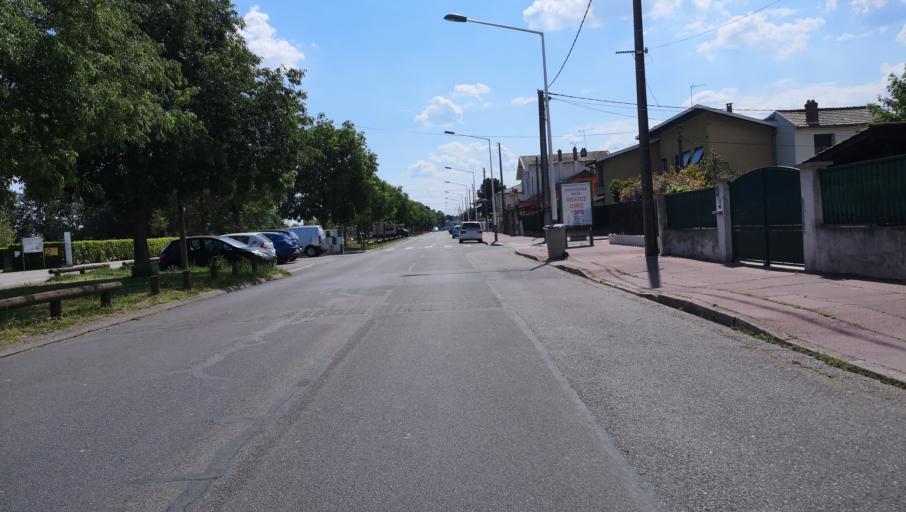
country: FR
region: Rhone-Alpes
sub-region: Departement du Rhone
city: Bron
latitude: 45.7211
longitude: 4.8937
